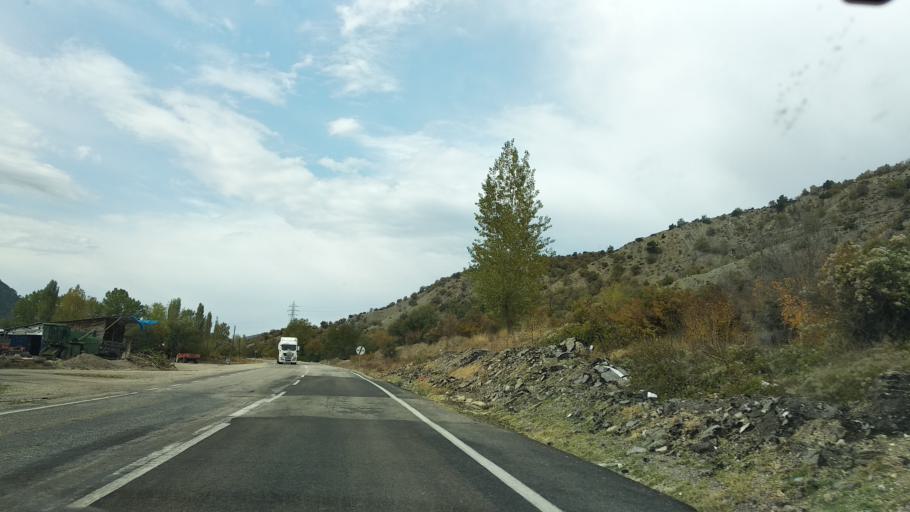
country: TR
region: Ankara
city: Nallihan
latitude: 40.3080
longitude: 31.2871
